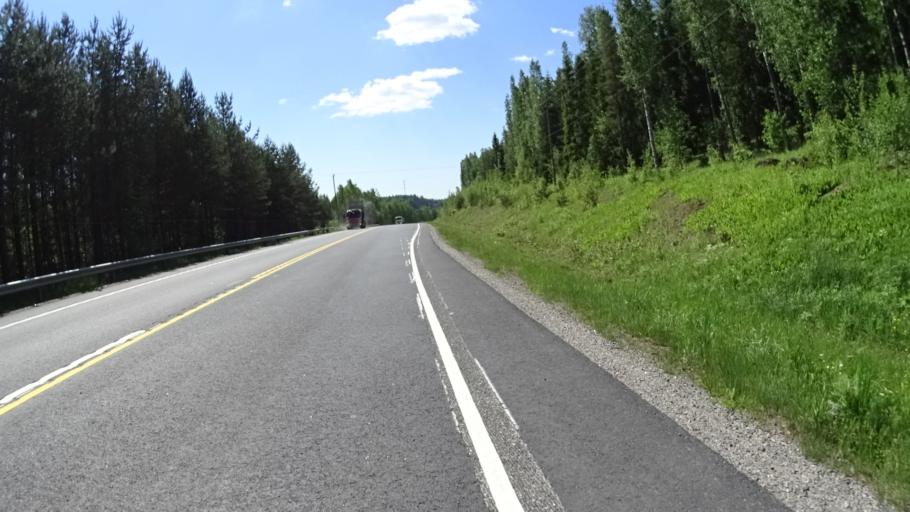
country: FI
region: Uusimaa
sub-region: Helsinki
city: Nurmijaervi
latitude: 60.4142
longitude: 24.8238
